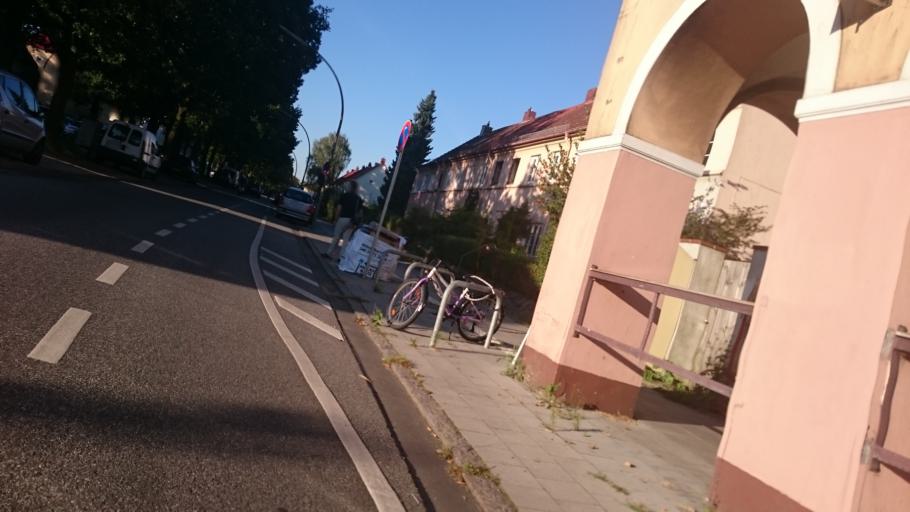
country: DE
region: Hamburg
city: Eidelstedt
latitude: 53.5680
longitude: 9.8889
